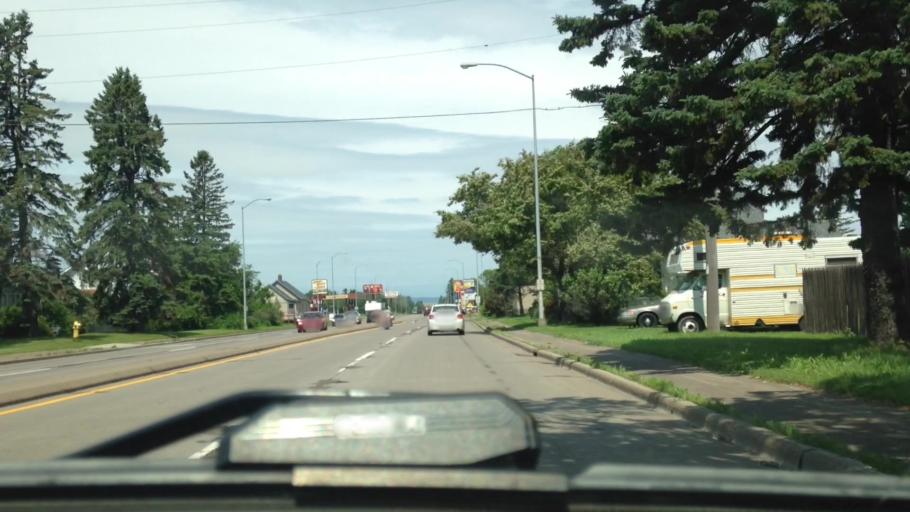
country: US
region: Wisconsin
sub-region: Douglas County
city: Superior
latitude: 46.6767
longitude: -92.0090
